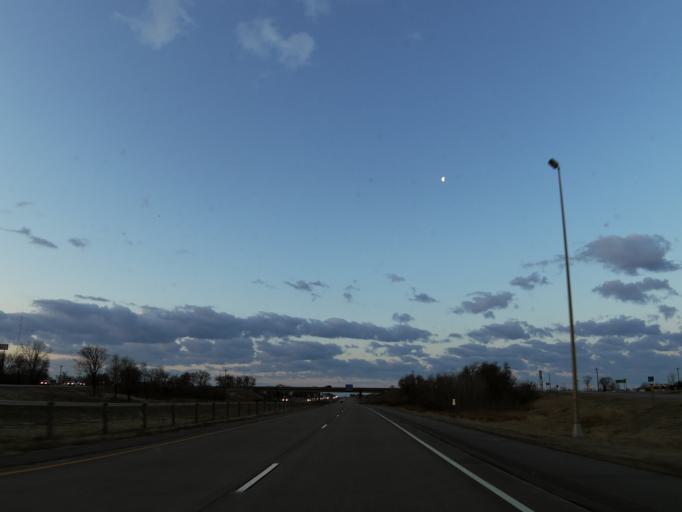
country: US
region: Minnesota
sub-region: Scott County
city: Elko New Market
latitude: 44.5755
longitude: -93.2985
